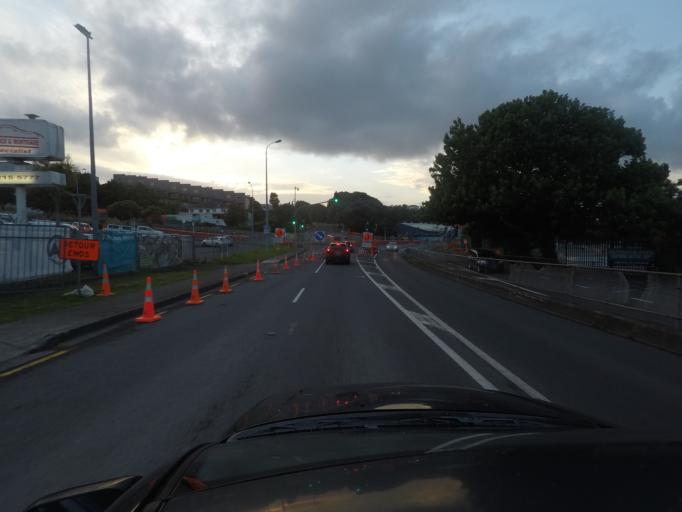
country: NZ
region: Auckland
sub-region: Auckland
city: Tamaki
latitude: -36.9005
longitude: 174.8534
